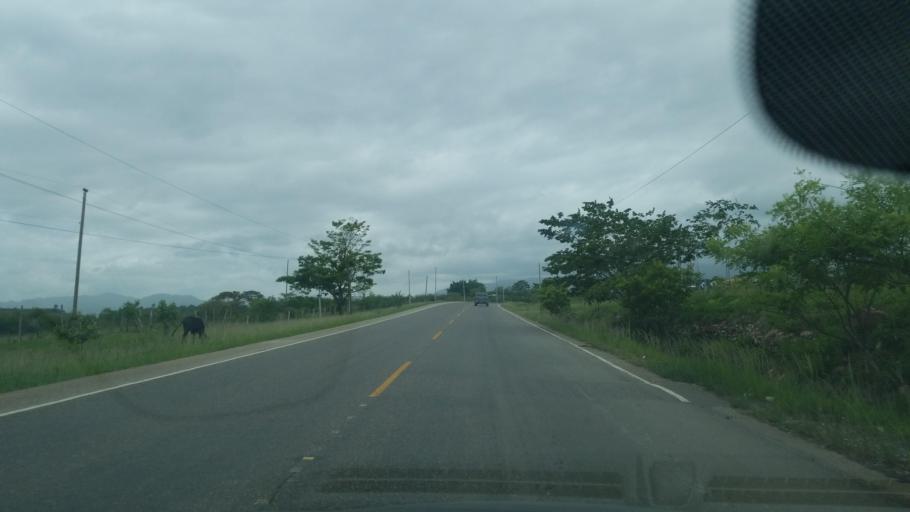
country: HN
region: Ocotepeque
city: Sensenti
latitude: 14.5150
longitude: -88.9517
